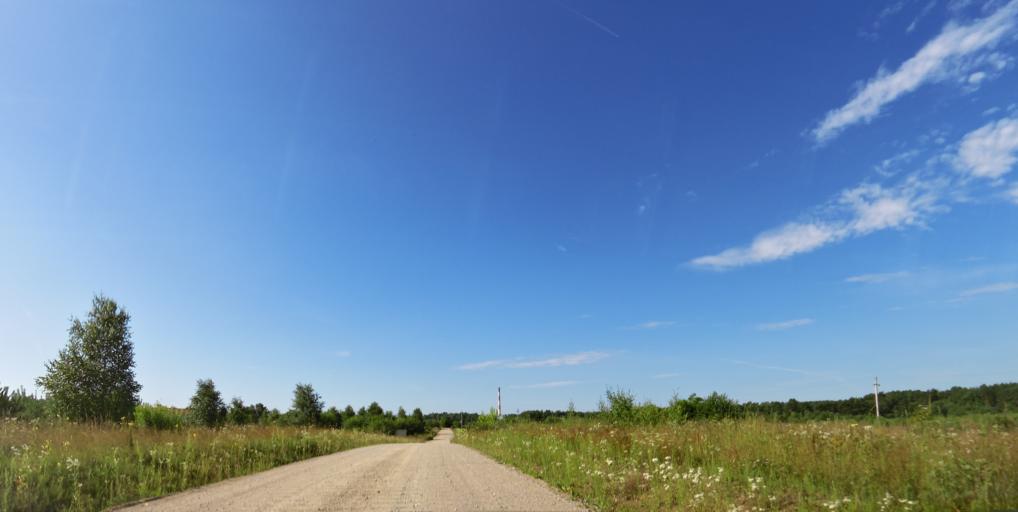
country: LT
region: Vilnius County
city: Pilaite
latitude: 54.6908
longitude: 25.1794
